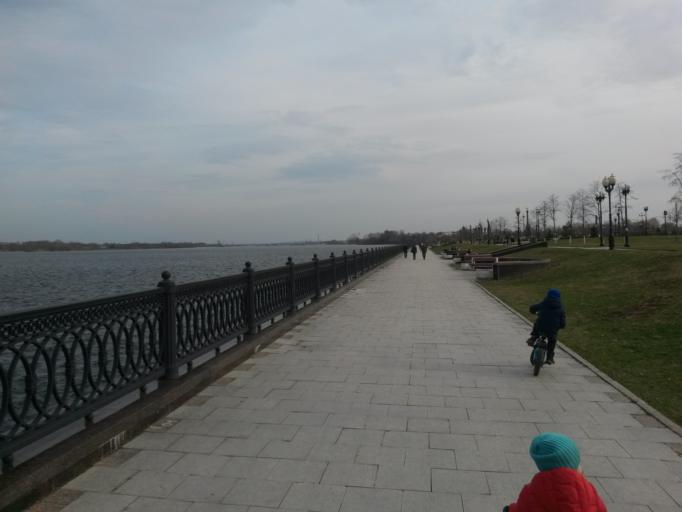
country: RU
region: Jaroslavl
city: Yaroslavl
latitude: 57.6213
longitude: 39.9049
